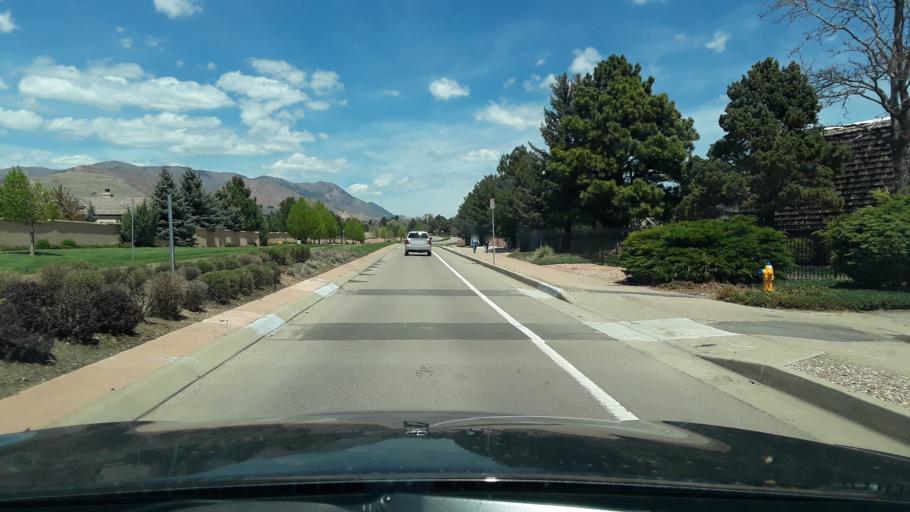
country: US
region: Colorado
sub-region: El Paso County
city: Manitou Springs
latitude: 38.8742
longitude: -104.8645
